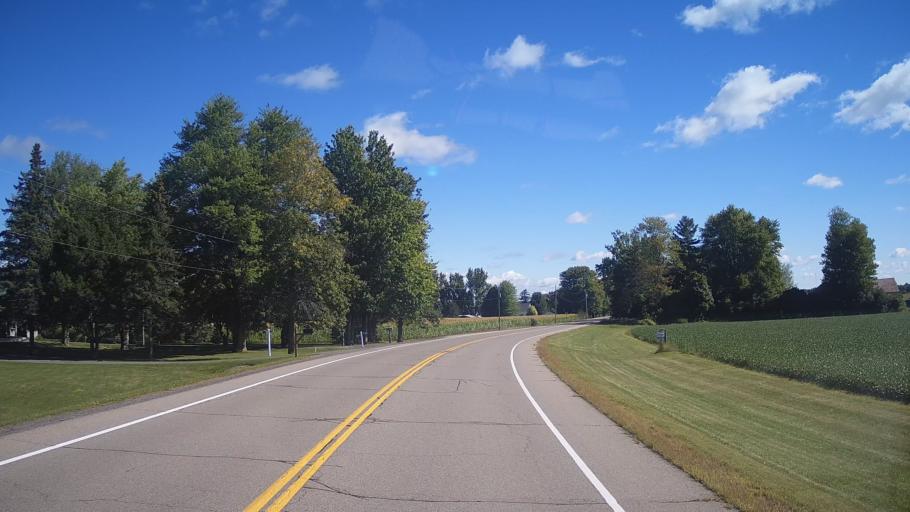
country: US
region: New York
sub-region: St. Lawrence County
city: Norfolk
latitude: 44.9626
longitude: -75.2817
